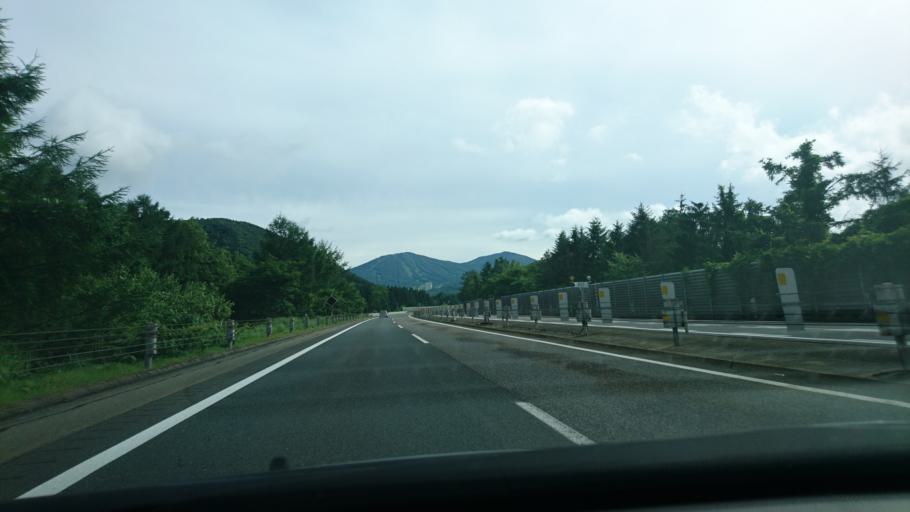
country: JP
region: Akita
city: Hanawa
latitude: 40.0384
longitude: 140.9907
